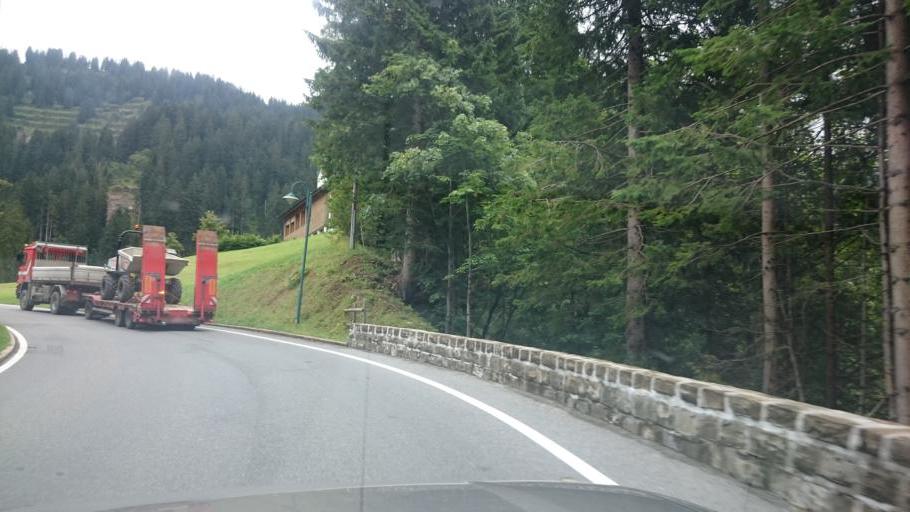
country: AT
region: Vorarlberg
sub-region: Politischer Bezirk Bregenz
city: Schroecken
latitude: 47.2582
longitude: 10.0909
